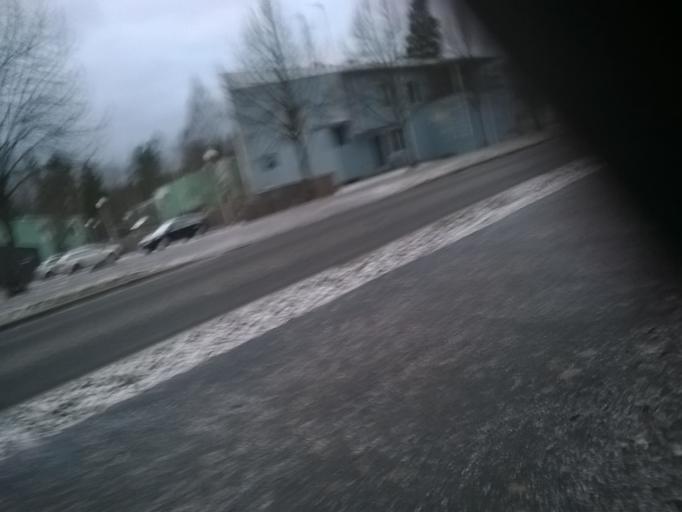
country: FI
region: Uusimaa
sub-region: Helsinki
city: Teekkarikylae
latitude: 60.2558
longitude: 24.8975
